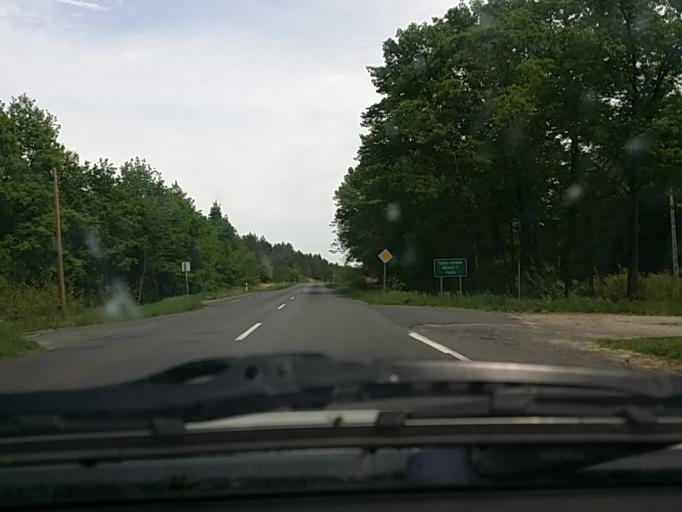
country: HU
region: Somogy
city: Barcs
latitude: 45.9679
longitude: 17.5260
